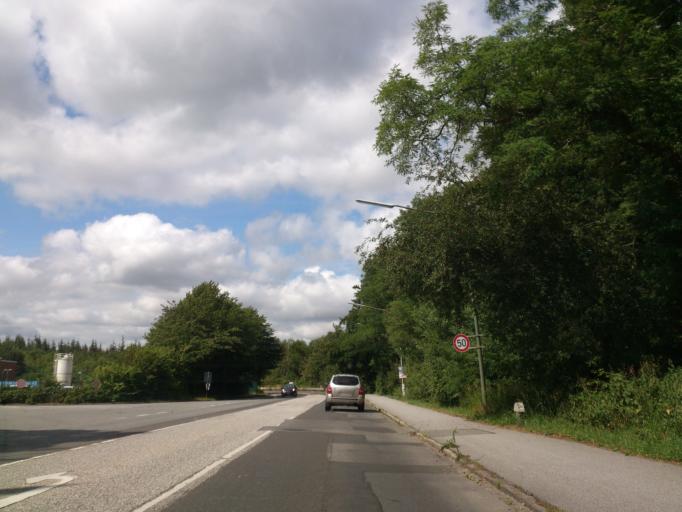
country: DE
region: Schleswig-Holstein
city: Flensburg
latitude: 54.8153
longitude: 9.4219
